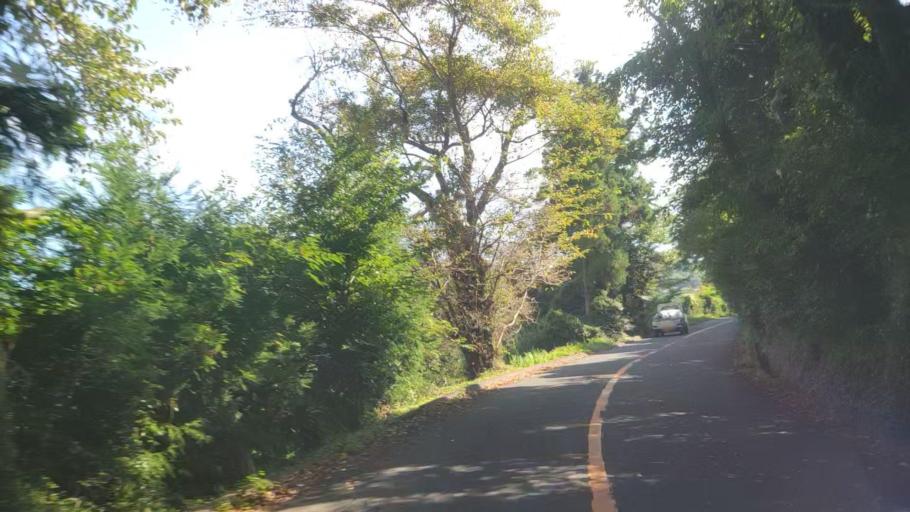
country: JP
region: Shizuoka
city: Shizuoka-shi
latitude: 34.9806
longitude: 138.4770
